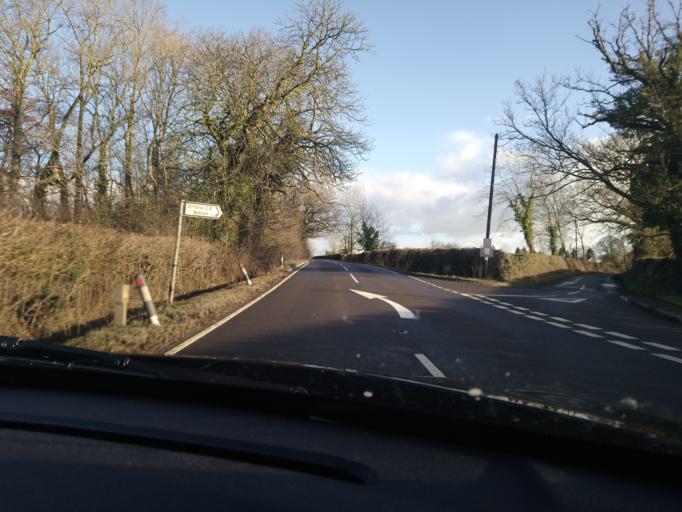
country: GB
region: Wales
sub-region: Wrexham
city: Overton
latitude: 52.9262
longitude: -2.9493
